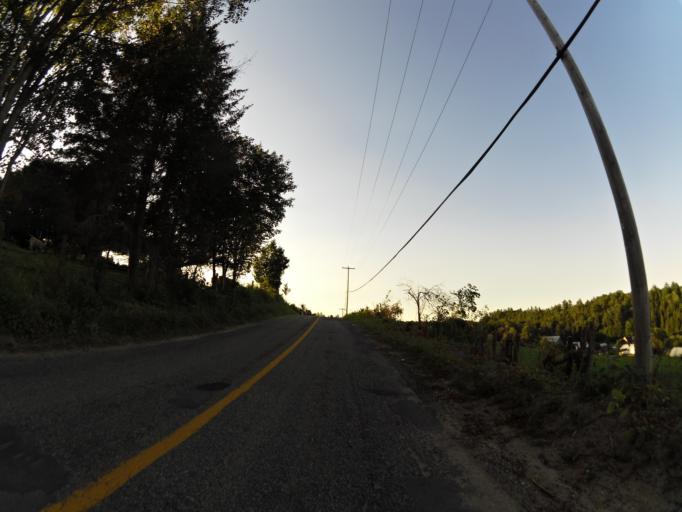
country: CA
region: Quebec
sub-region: Outaouais
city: Wakefield
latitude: 45.7343
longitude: -75.9733
